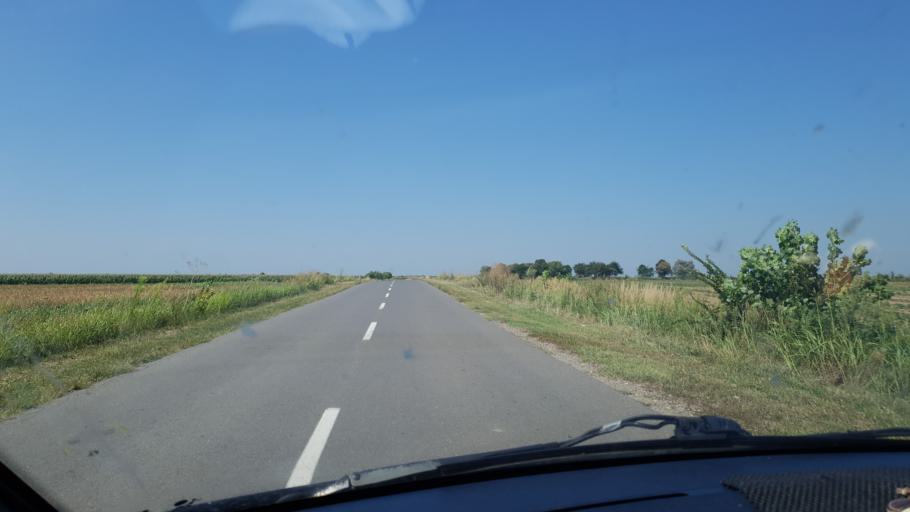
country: RS
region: Autonomna Pokrajina Vojvodina
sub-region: Juznobacki Okrug
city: Kovilj
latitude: 45.2121
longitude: 20.0643
